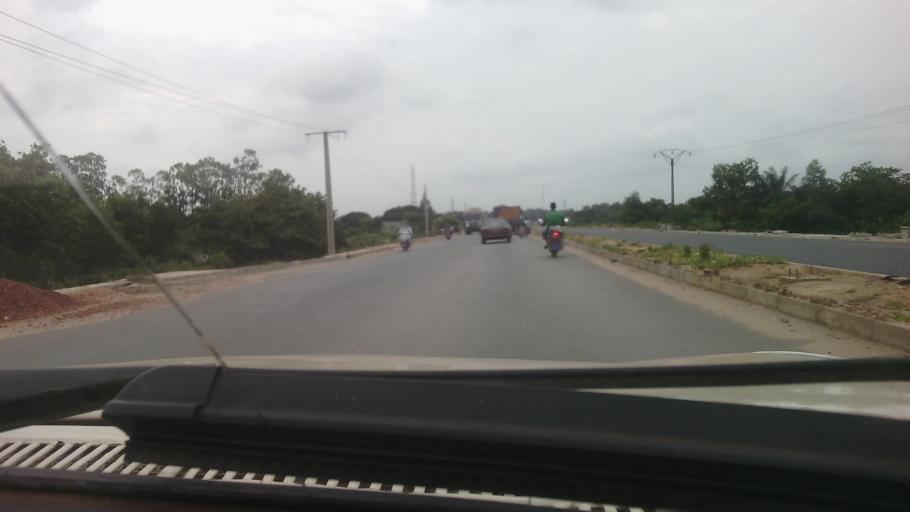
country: BJ
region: Atlantique
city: Ouidah
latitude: 6.3802
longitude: 2.1659
